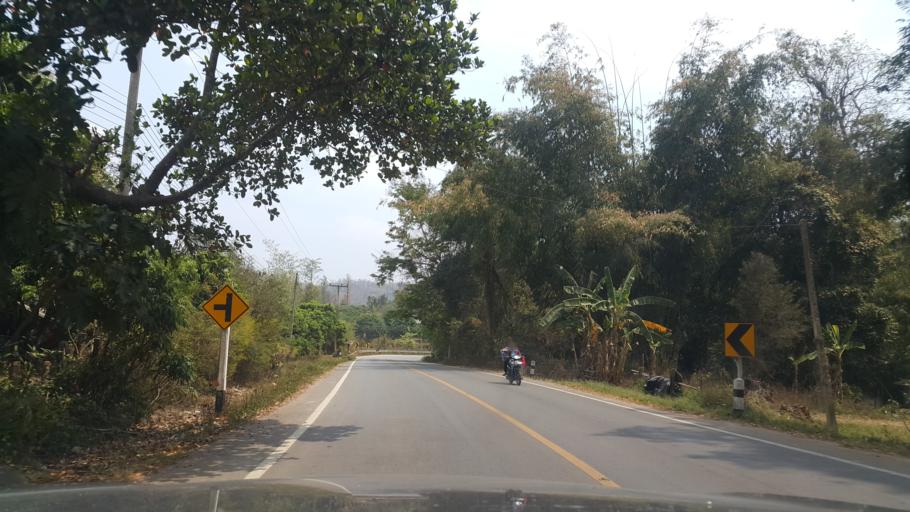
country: TH
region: Lamphun
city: Thung Hua Chang
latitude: 18.1245
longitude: 99.0136
